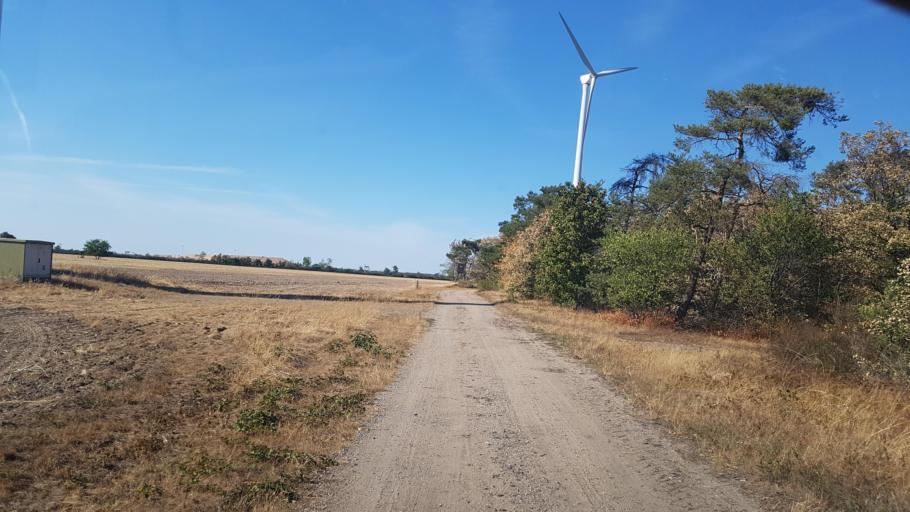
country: DE
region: Brandenburg
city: Muhlberg
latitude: 51.4097
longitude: 13.2848
